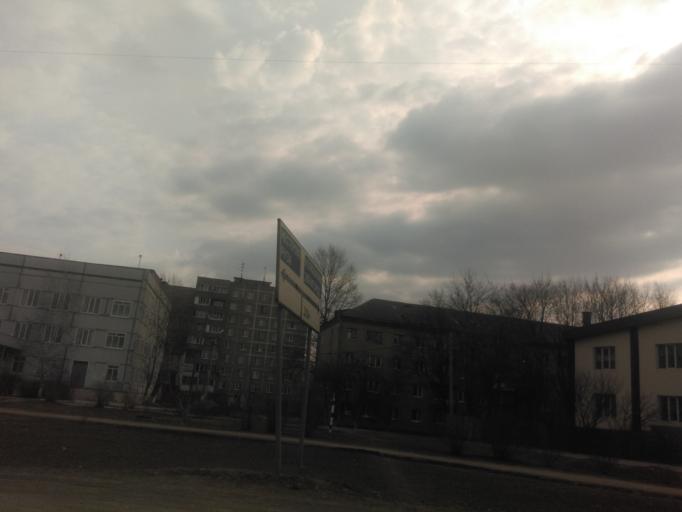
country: RU
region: Moskovskaya
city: Tuchkovo
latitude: 55.6004
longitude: 36.4834
